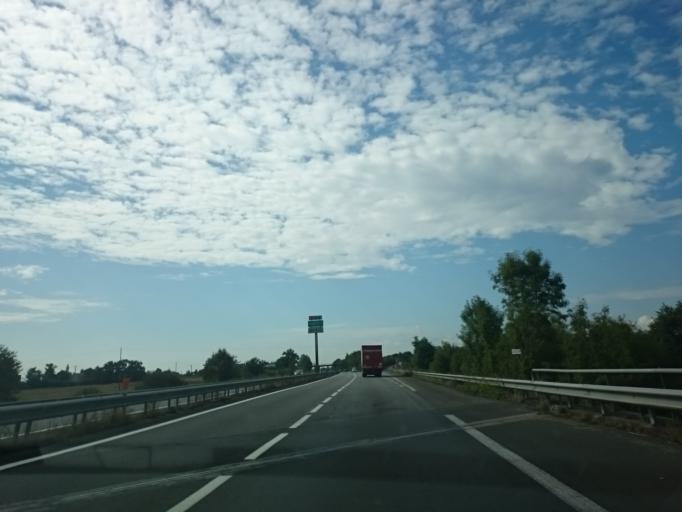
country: FR
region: Pays de la Loire
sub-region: Departement de la Loire-Atlantique
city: Heric
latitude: 47.4517
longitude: -1.6414
